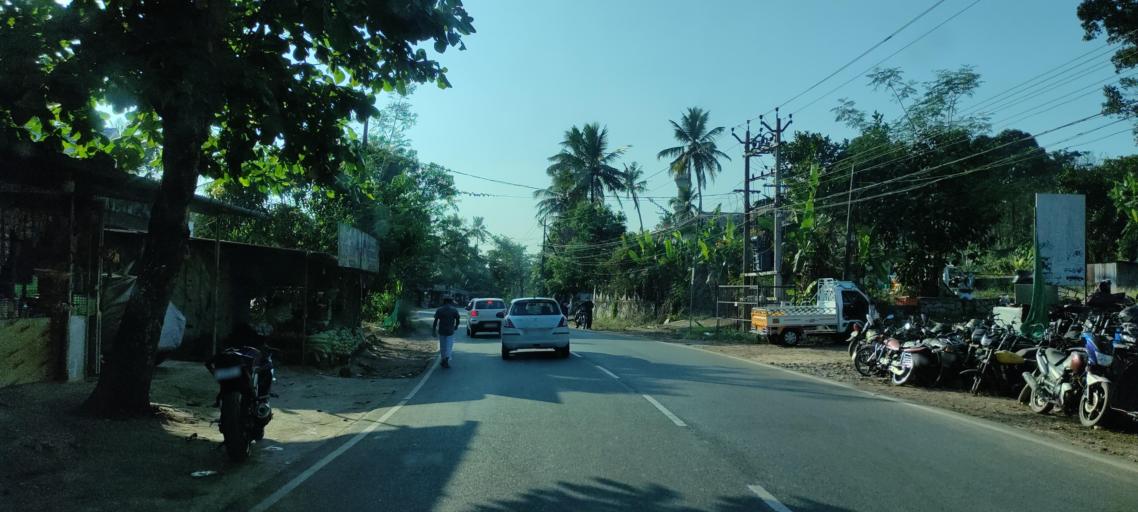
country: IN
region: Kerala
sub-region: Pattanamtitta
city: Adur
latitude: 9.1662
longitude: 76.6818
